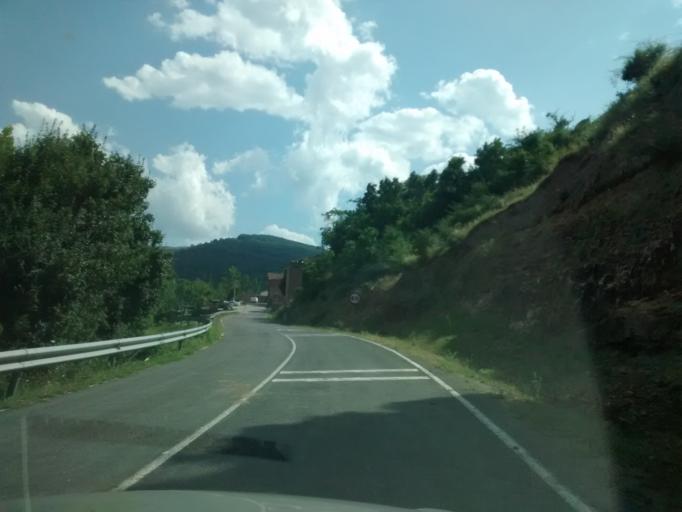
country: ES
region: La Rioja
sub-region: Provincia de La Rioja
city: Ajamil
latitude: 42.1693
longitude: -2.4855
